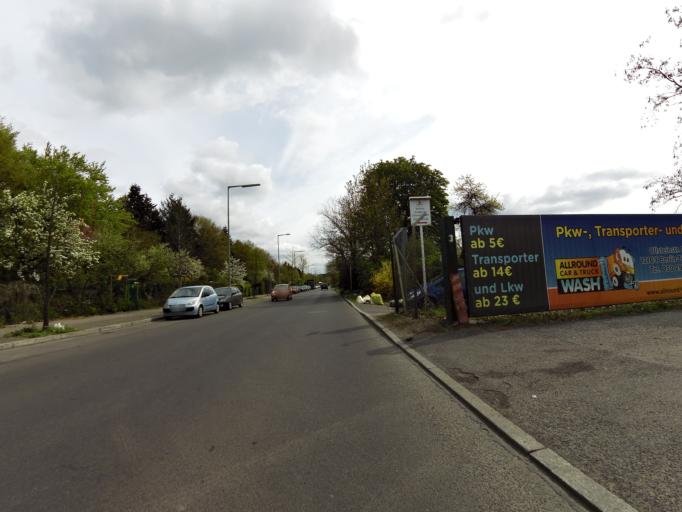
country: DE
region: Berlin
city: Tempelhof Bezirk
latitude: 52.4528
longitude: 13.4004
